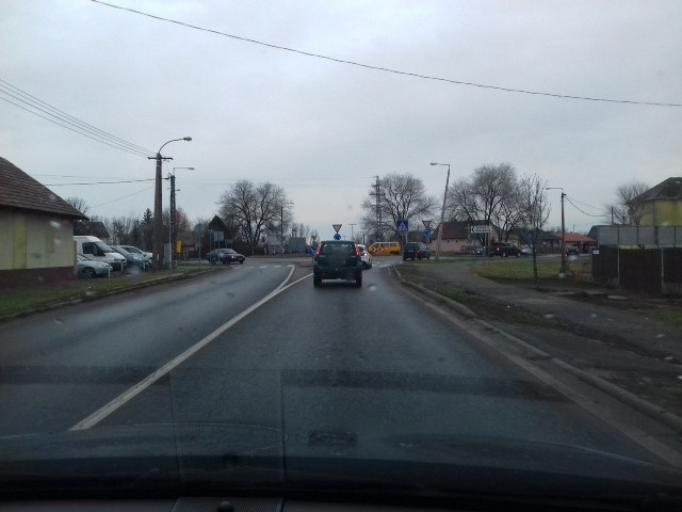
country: HU
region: Szabolcs-Szatmar-Bereg
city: Ujfeherto
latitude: 47.8128
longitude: 21.7018
